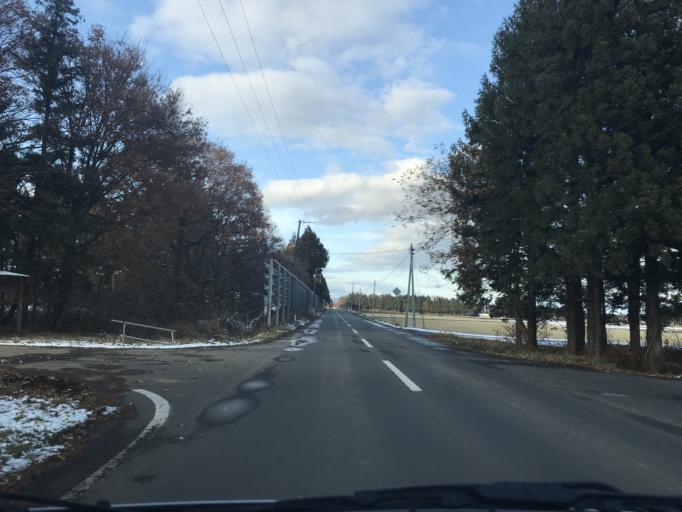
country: JP
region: Iwate
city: Kitakami
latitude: 39.2468
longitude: 141.0326
